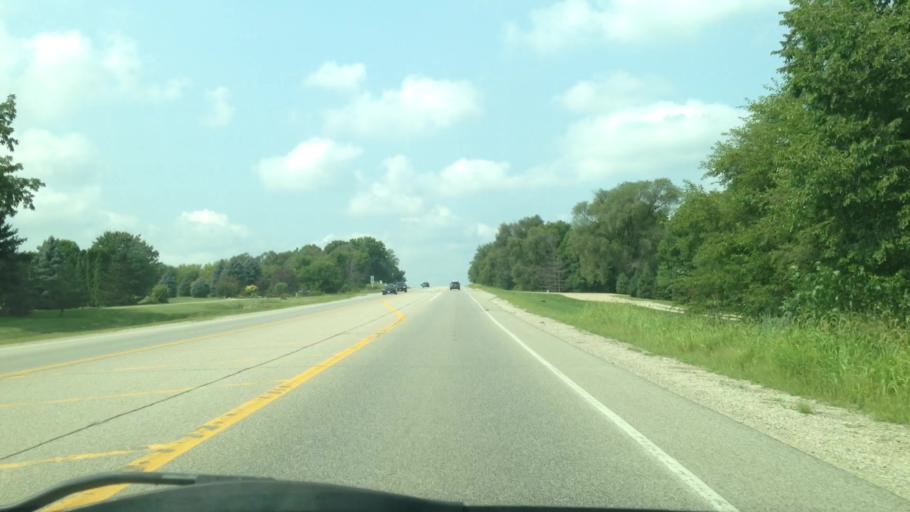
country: US
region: Iowa
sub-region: Linn County
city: Fairfax
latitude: 41.9372
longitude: -91.7601
